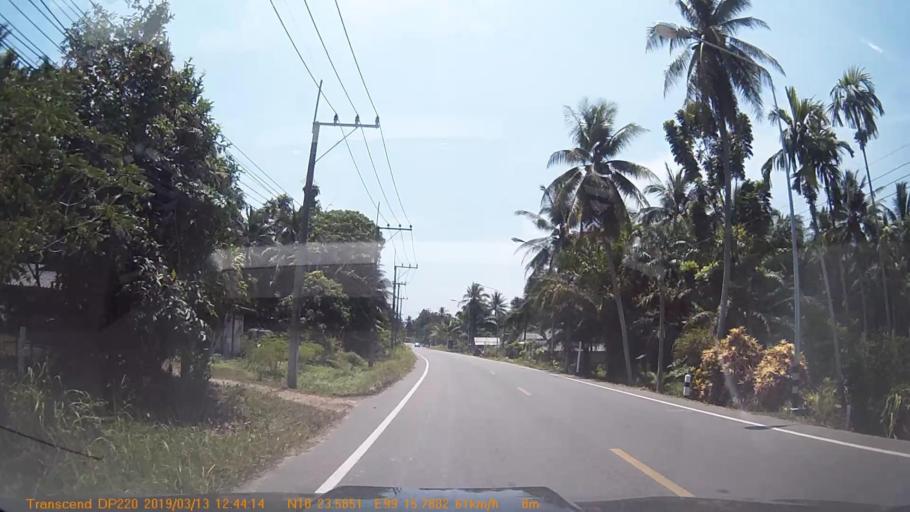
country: TH
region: Chumphon
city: Chumphon
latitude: 10.3928
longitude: 99.2630
